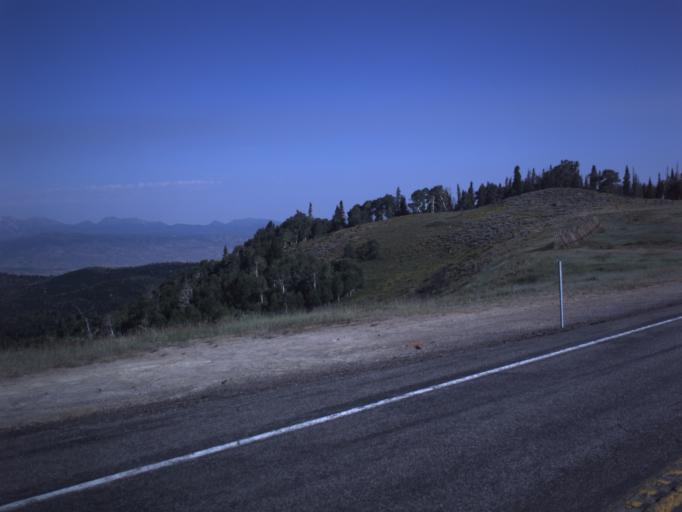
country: US
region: Utah
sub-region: Sanpete County
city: Fairview
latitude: 39.6384
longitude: -111.3298
